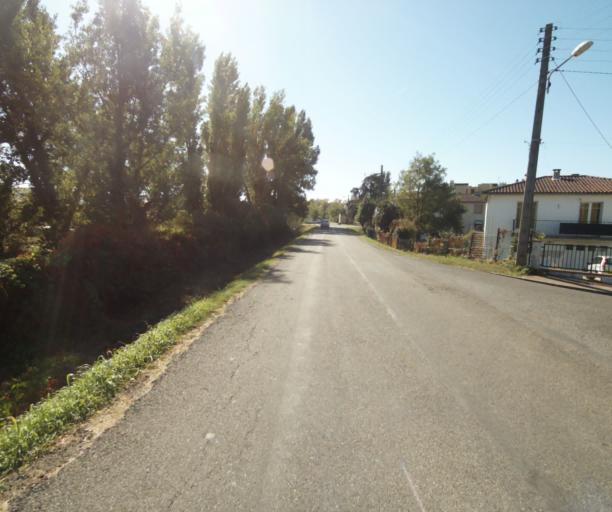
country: FR
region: Midi-Pyrenees
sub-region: Departement du Tarn-et-Garonne
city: Moissac
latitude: 44.1008
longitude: 1.1021
